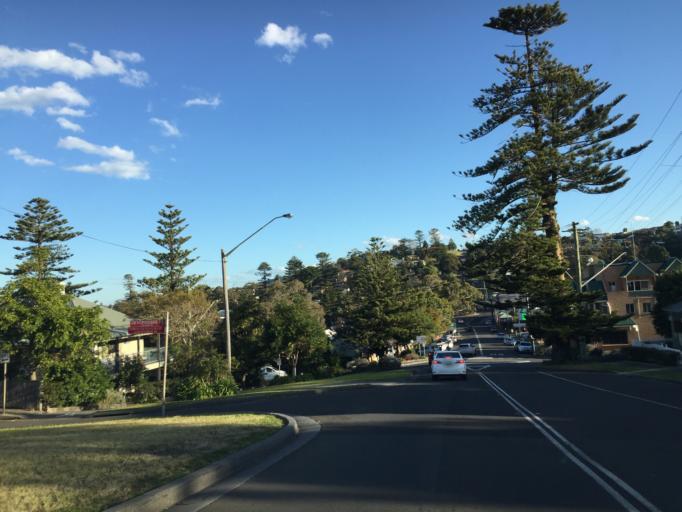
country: AU
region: New South Wales
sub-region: Kiama
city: Kiama
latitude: -34.6671
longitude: 150.8546
